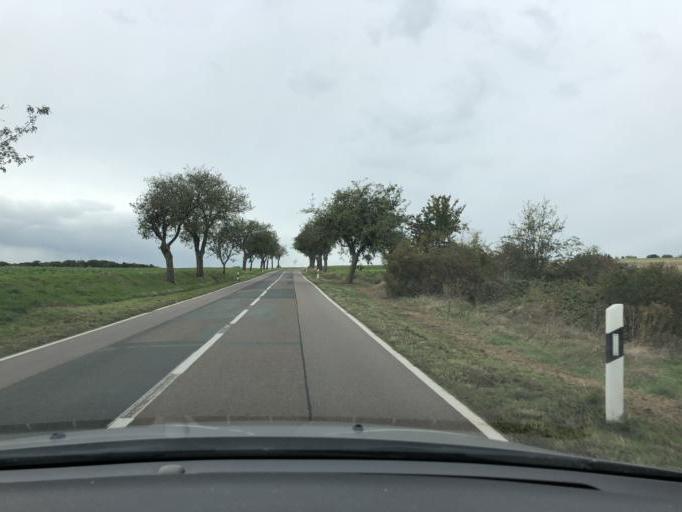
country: DE
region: Saxony-Anhalt
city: Bad Kosen
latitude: 51.1575
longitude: 11.7364
